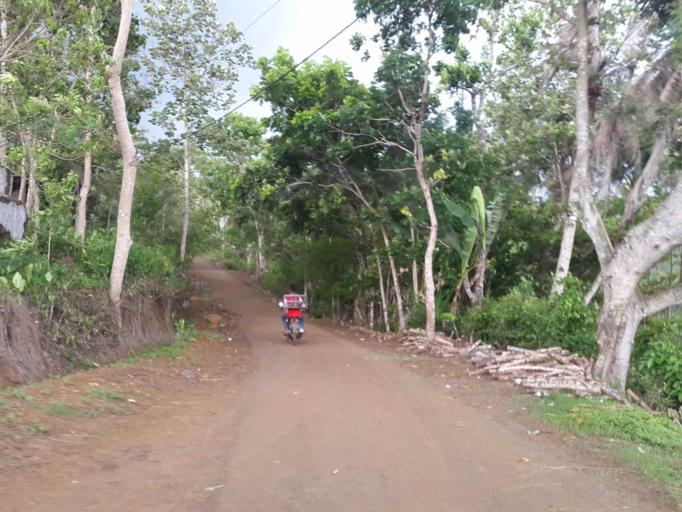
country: ID
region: Central Java
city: Limbangan
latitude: -7.2912
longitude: 108.7017
